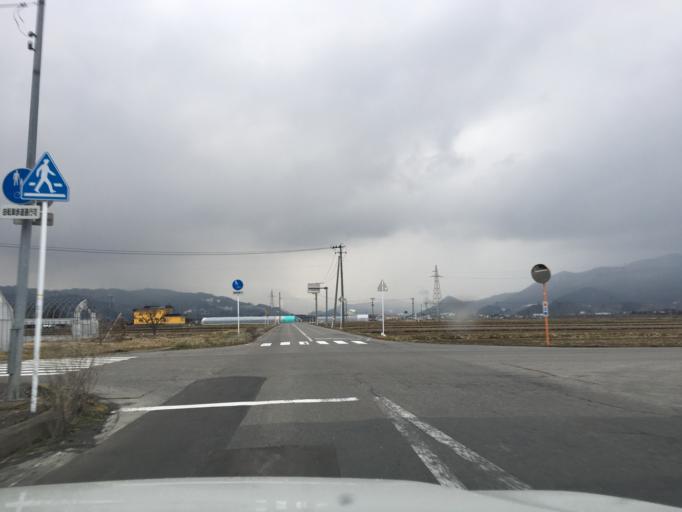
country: JP
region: Aomori
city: Hirosaki
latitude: 40.5656
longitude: 140.5500
